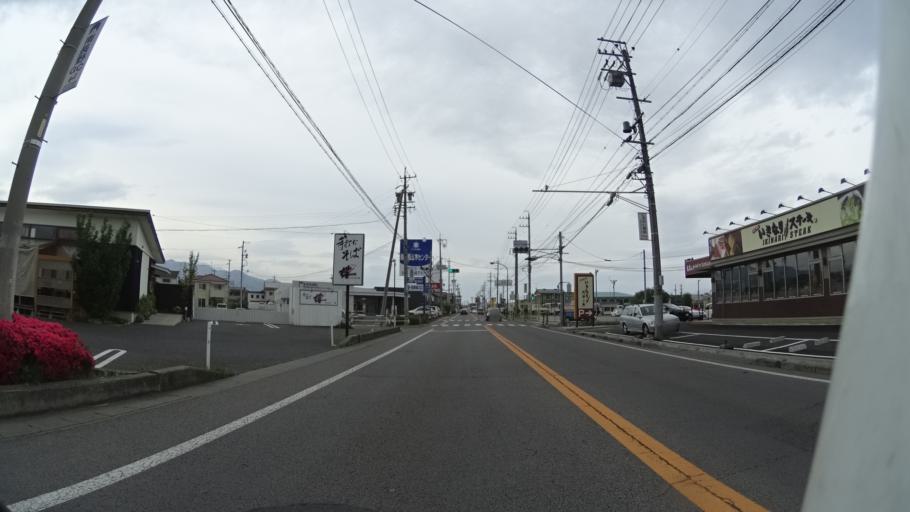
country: JP
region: Nagano
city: Nagano-shi
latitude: 36.5825
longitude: 138.1493
